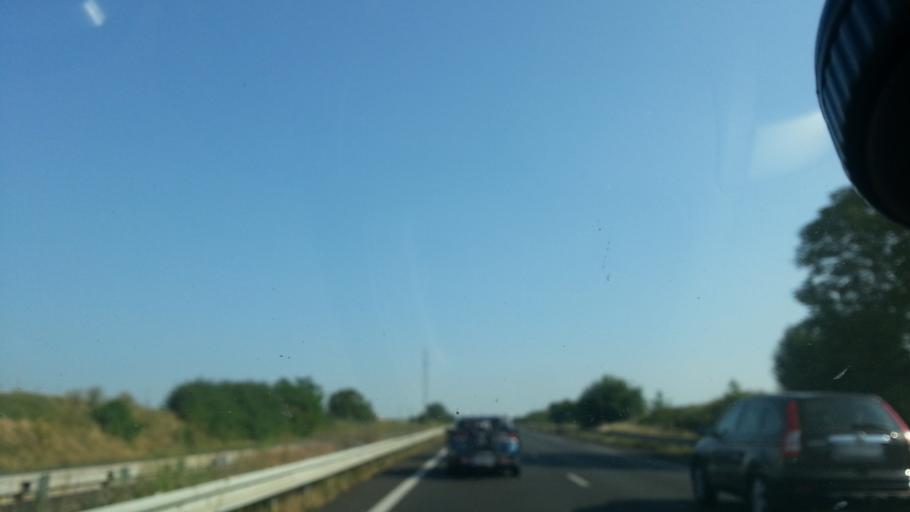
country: FR
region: Poitou-Charentes
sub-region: Departement de la Vienne
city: Les Ormes
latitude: 46.9796
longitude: 0.5469
